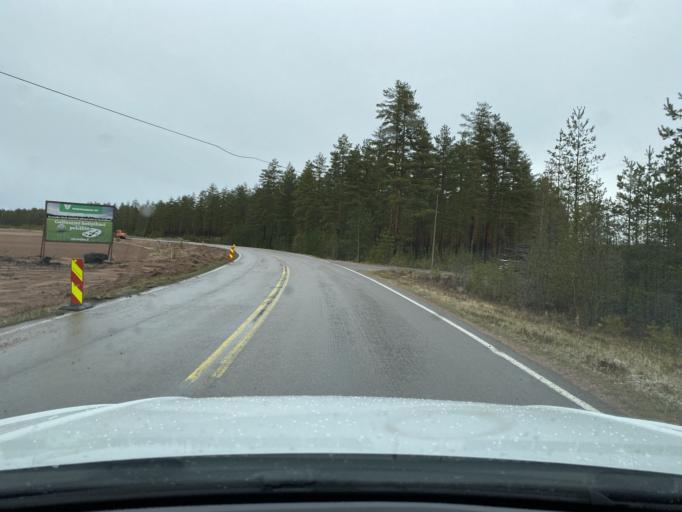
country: FI
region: Satakunta
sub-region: Pori
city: Vampula
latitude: 60.9607
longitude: 22.6768
